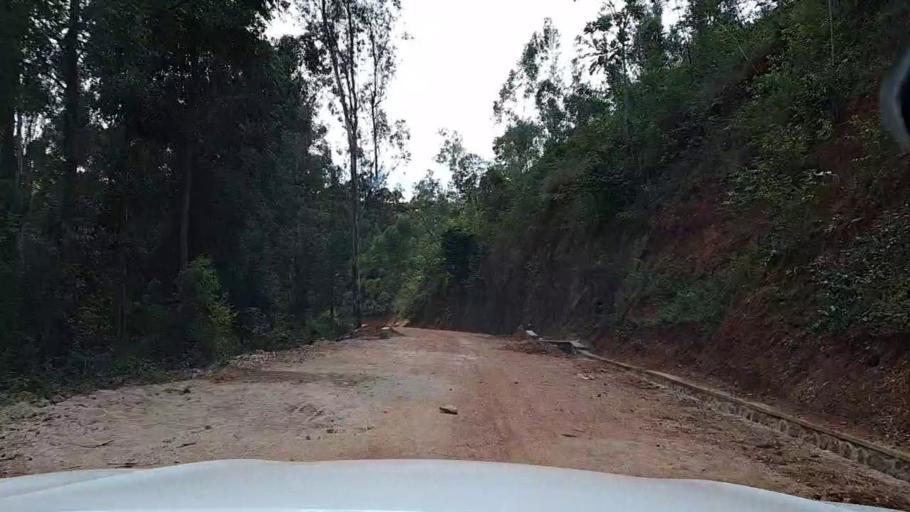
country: BI
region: Ngozi
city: Ngozi
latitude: -2.8117
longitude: 29.7303
